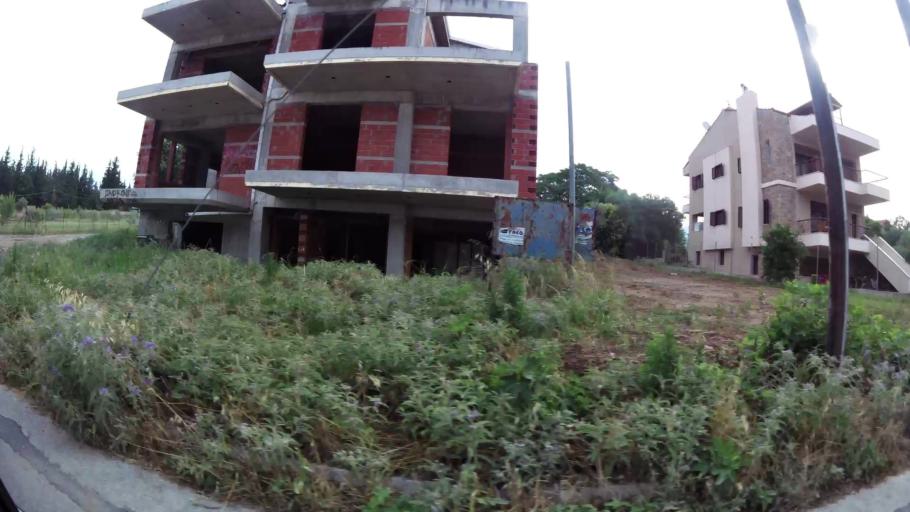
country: GR
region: Central Macedonia
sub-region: Nomos Thessalonikis
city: Thermi
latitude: 40.5515
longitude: 23.0253
